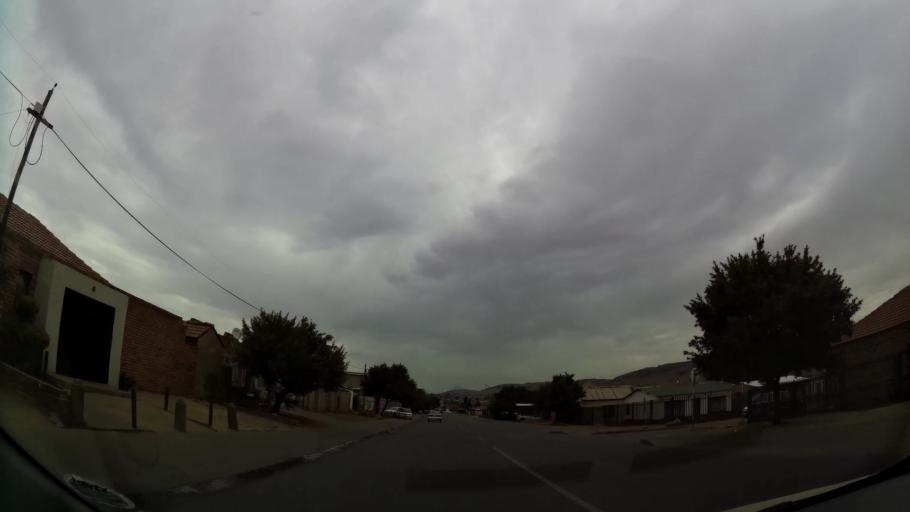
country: ZA
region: Gauteng
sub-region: City of Tshwane Metropolitan Municipality
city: Cullinan
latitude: -25.7093
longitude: 28.3580
